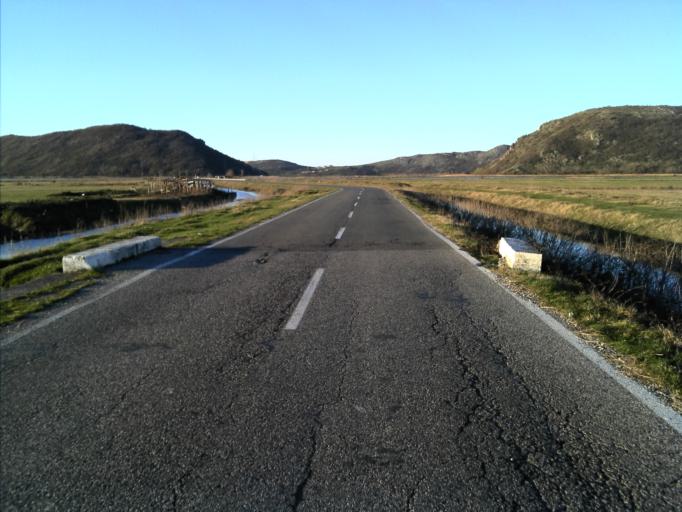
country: AL
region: Shkoder
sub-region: Rrethi i Shkodres
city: Dajc
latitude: 41.9407
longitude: 19.4449
